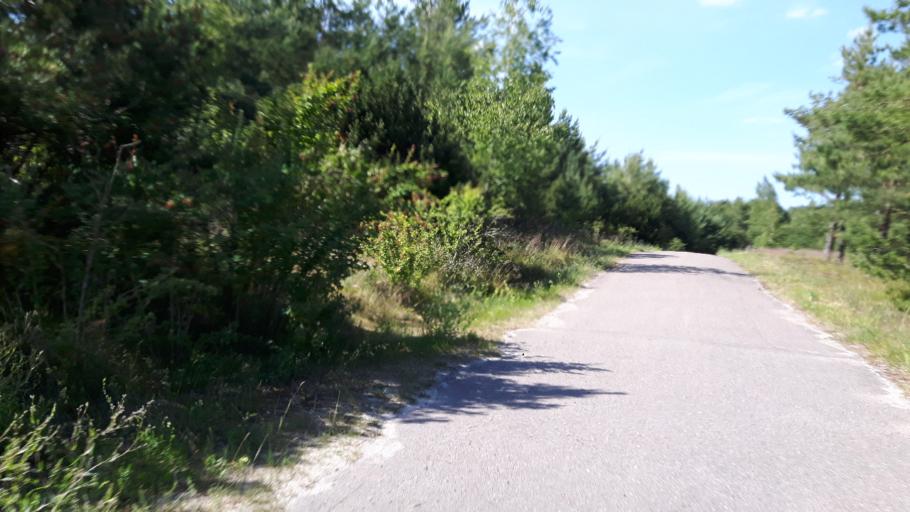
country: LT
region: Klaipedos apskritis
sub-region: Klaipeda
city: Klaipeda
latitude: 55.6909
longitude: 21.1030
